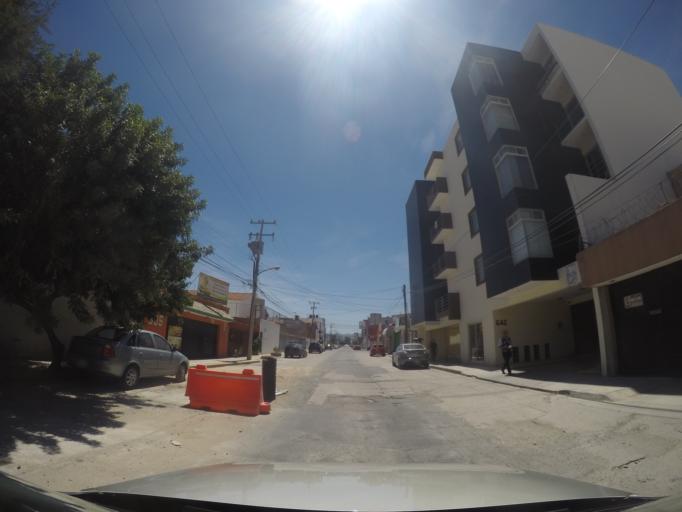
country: MX
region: San Luis Potosi
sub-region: San Luis Potosi
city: San Luis Potosi
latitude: 22.1557
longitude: -100.9956
